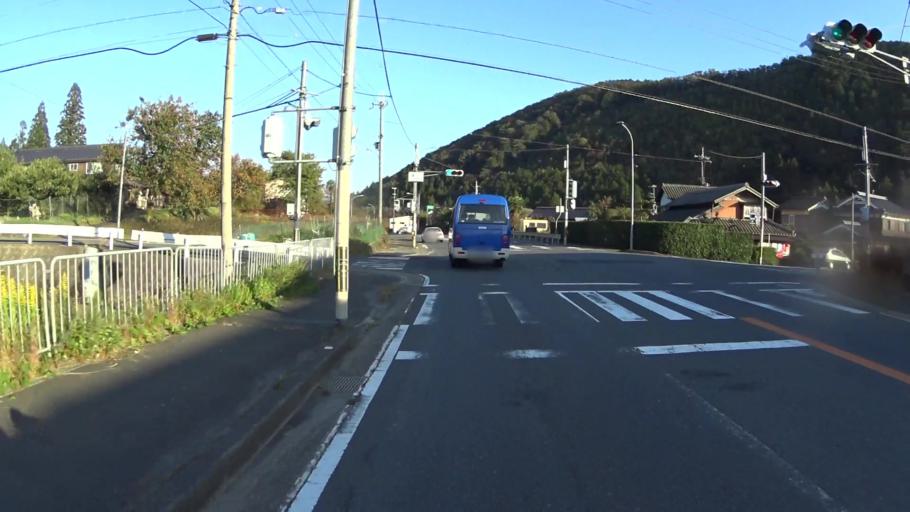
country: JP
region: Kyoto
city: Ayabe
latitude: 35.1801
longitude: 135.3794
